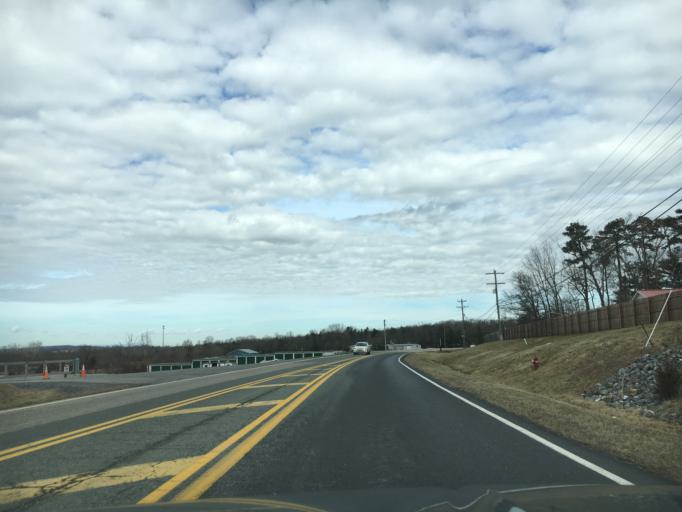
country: US
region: Virginia
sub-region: Augusta County
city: Crimora
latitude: 38.1374
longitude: -78.8452
